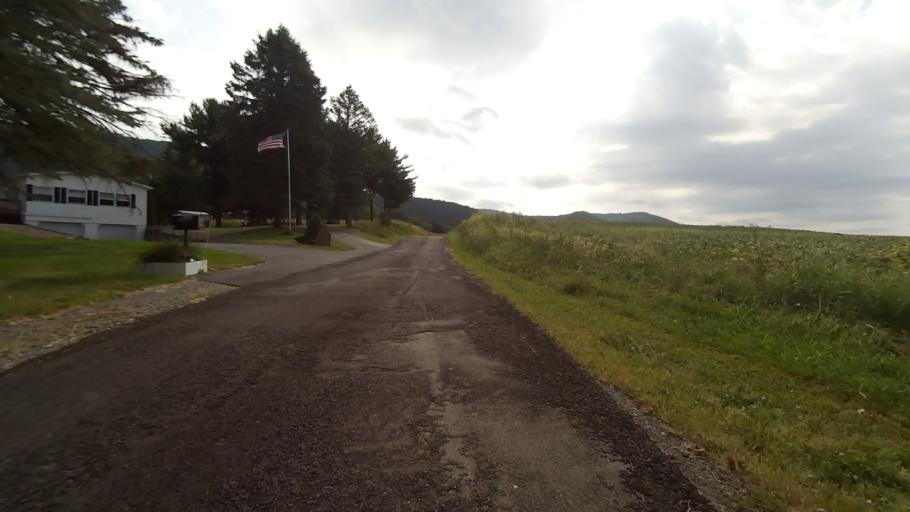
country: US
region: Pennsylvania
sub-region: Blair County
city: Williamsburg
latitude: 40.4933
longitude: -78.1743
